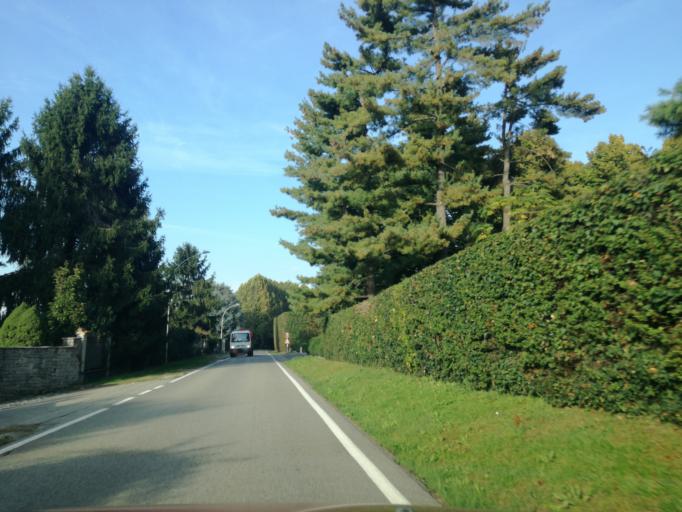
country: IT
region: Lombardy
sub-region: Provincia di Monza e Brianza
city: Sulbiate
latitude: 45.6523
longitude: 9.4236
